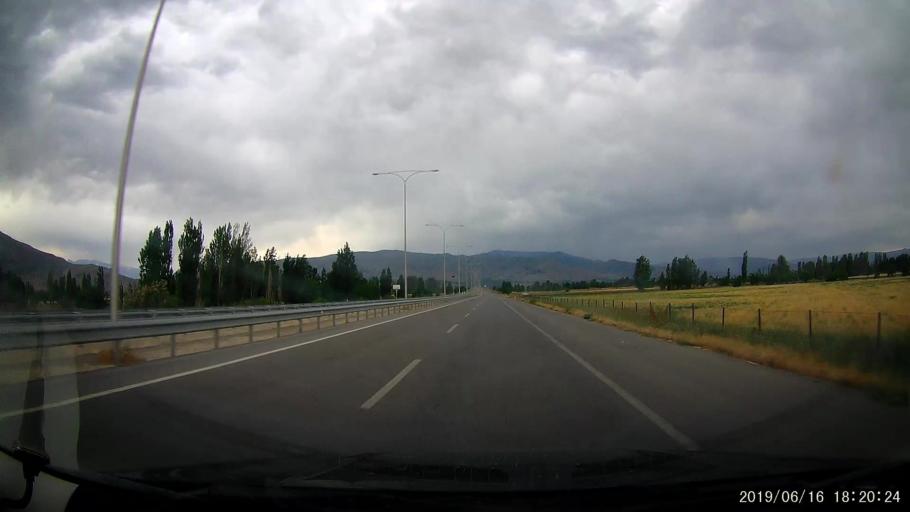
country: TR
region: Erzincan
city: Erzincan
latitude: 39.7197
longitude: 39.4700
